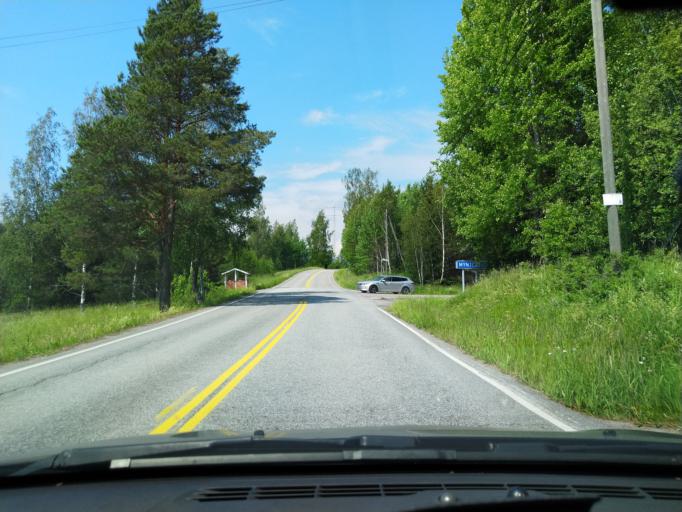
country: FI
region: Uusimaa
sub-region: Helsinki
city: Lohja
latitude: 60.3063
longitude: 24.0928
